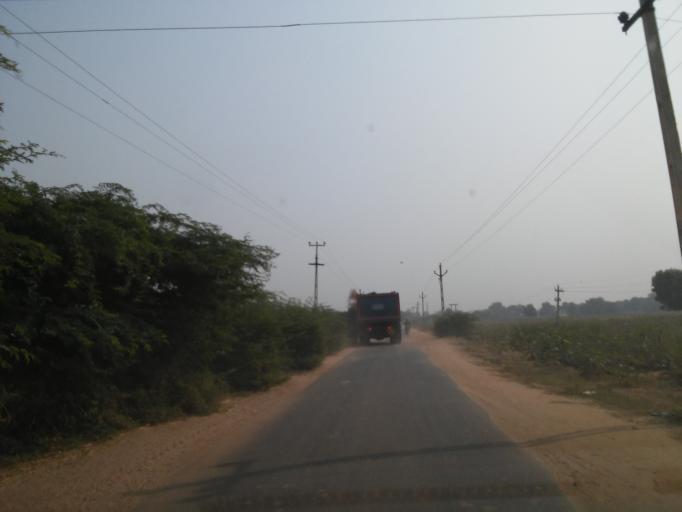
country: IN
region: Gujarat
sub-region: Kachchh
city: Bhuj
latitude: 23.4325
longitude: 69.7009
